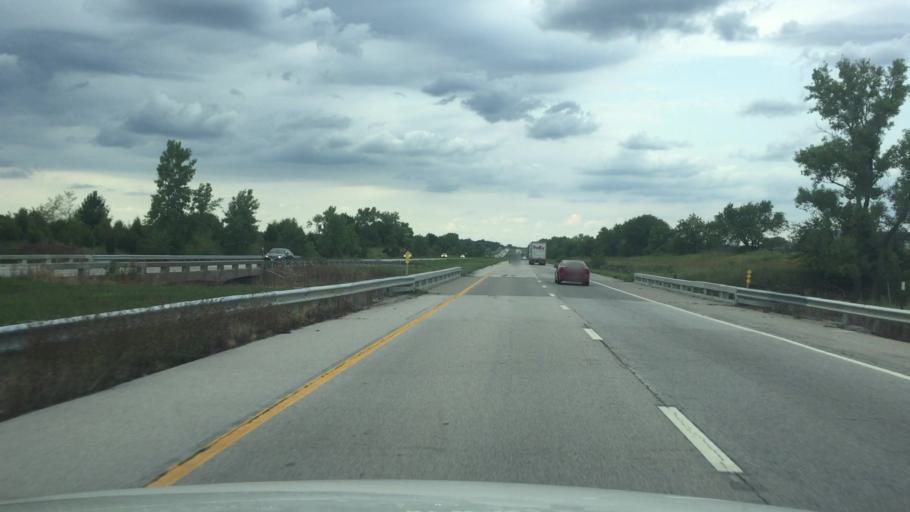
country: US
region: Kansas
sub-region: Miami County
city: Louisburg
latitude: 38.7523
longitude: -94.6774
